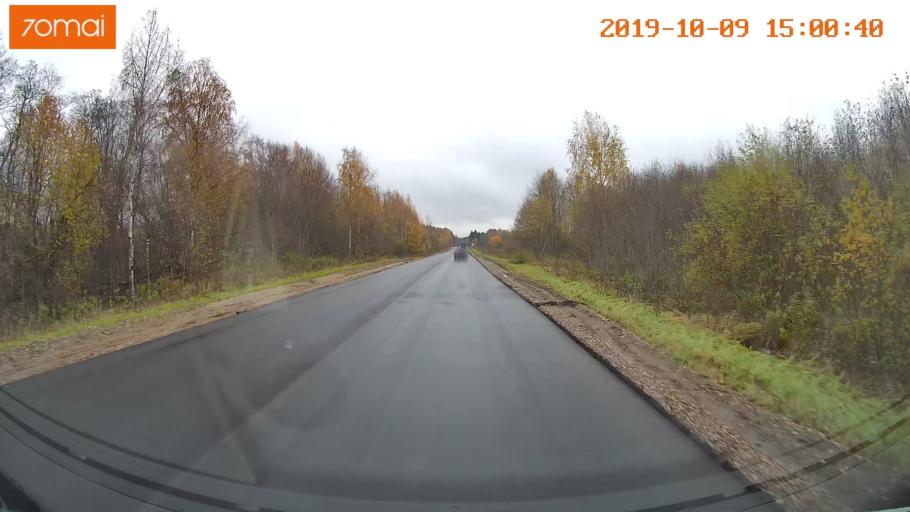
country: RU
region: Kostroma
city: Chistyye Bory
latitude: 58.3067
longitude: 41.6786
